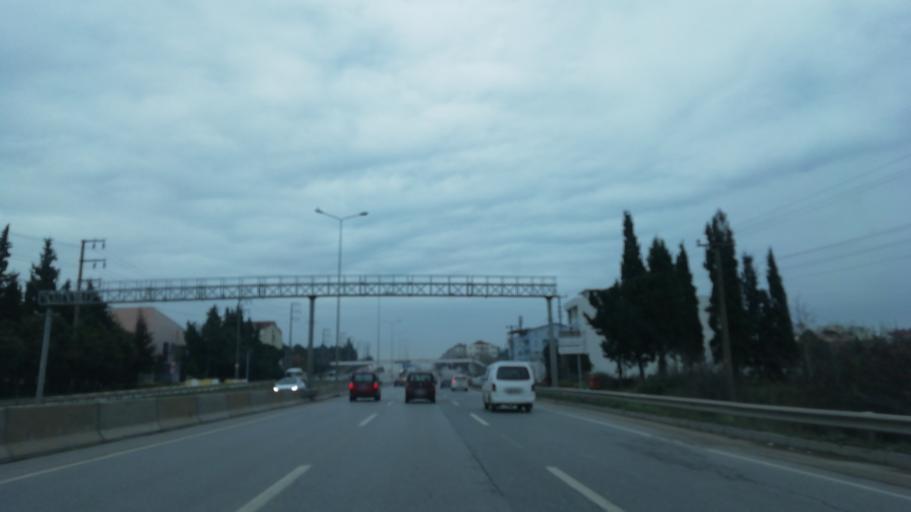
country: TR
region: Kocaeli
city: Derince
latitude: 40.7571
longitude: 29.8059
